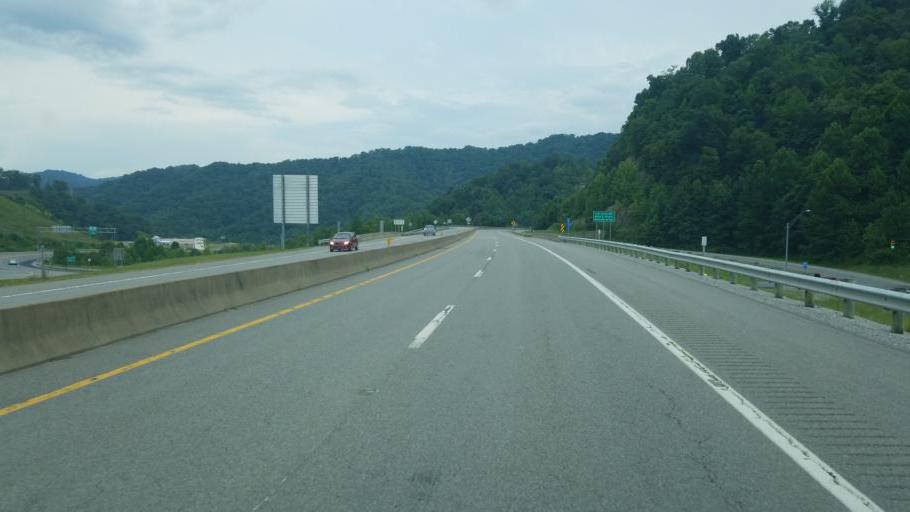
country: US
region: West Virginia
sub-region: Logan County
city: Mount Gay-Shamrock
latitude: 37.8557
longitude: -82.0457
